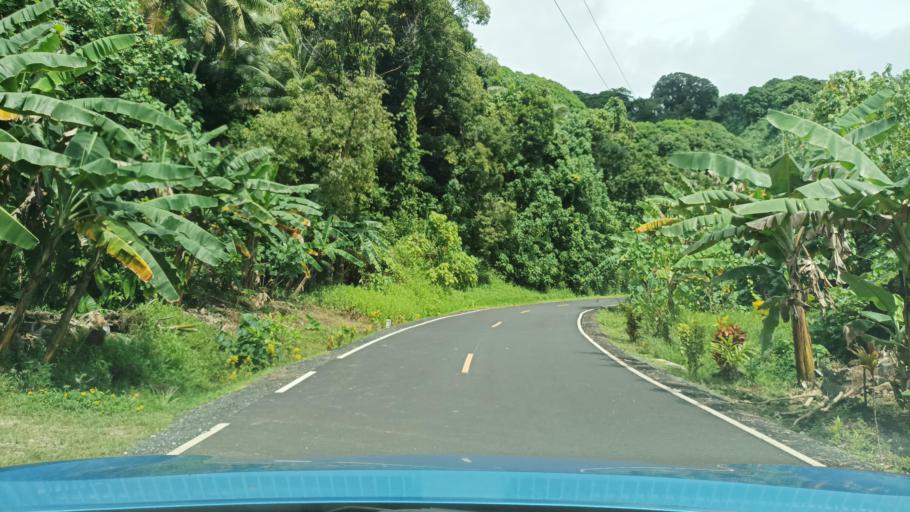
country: FM
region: Pohnpei
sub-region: Madolenihm Municipality
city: Madolenihm Municipality Government
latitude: 6.8700
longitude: 158.3289
